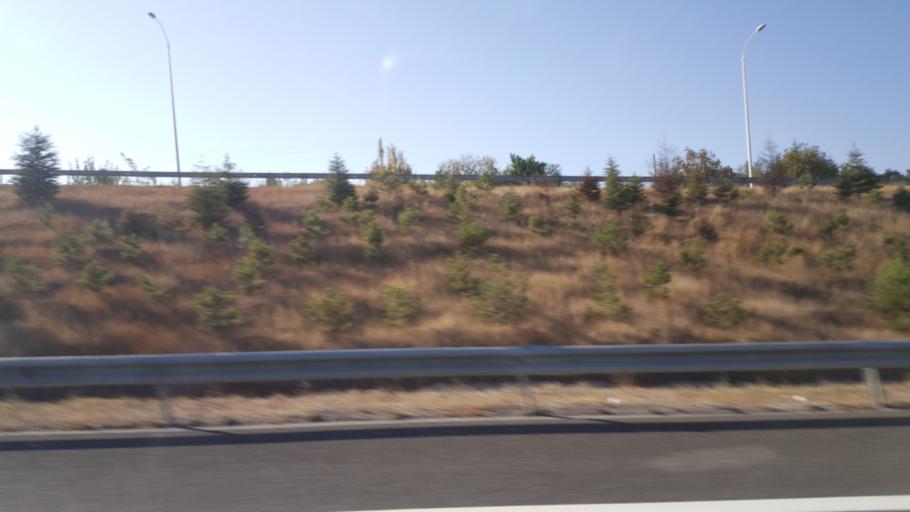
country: TR
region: Ankara
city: Mamak
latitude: 39.9023
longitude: 32.9804
